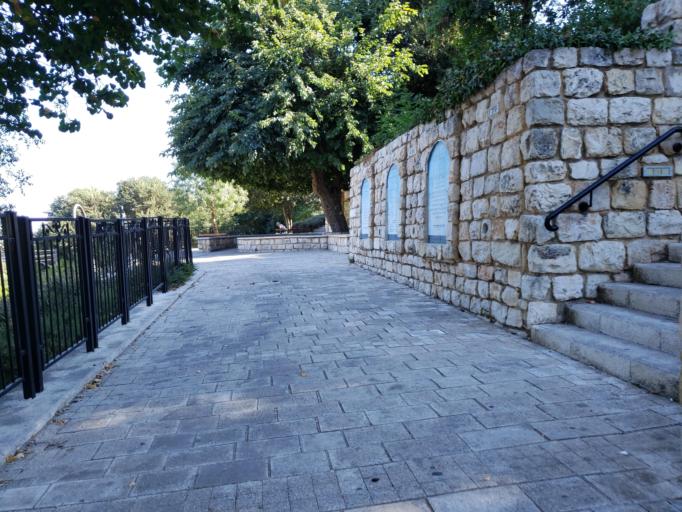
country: IL
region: Northern District
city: Safed
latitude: 32.9692
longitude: 35.4967
